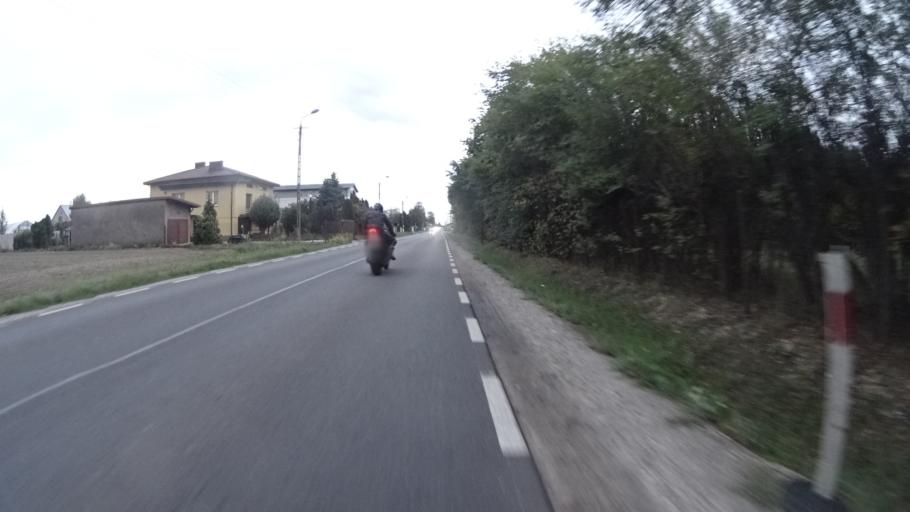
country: PL
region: Masovian Voivodeship
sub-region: Powiat warszawski zachodni
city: Ozarow Mazowiecki
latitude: 52.2312
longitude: 20.7689
